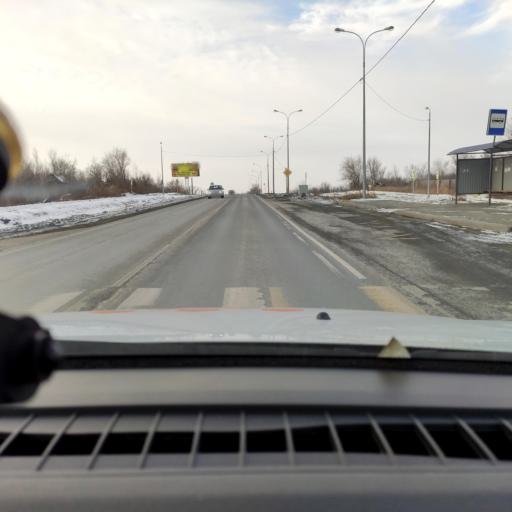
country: RU
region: Samara
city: Chapayevsk
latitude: 52.9965
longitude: 49.7385
